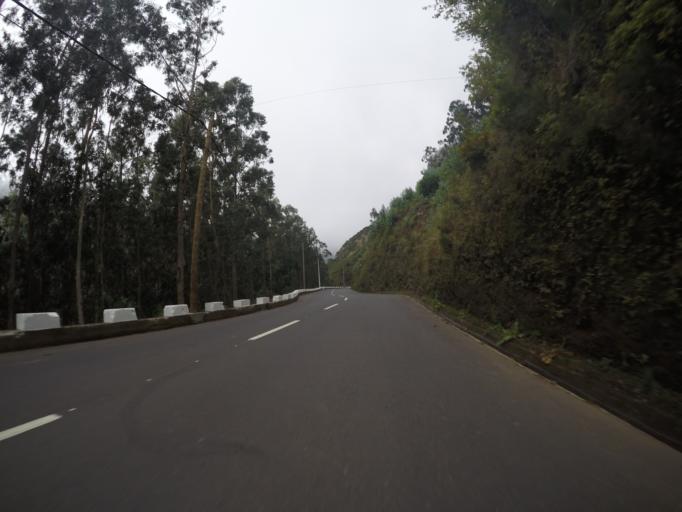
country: PT
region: Madeira
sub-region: Camara de Lobos
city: Curral das Freiras
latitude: 32.7000
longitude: -16.9530
